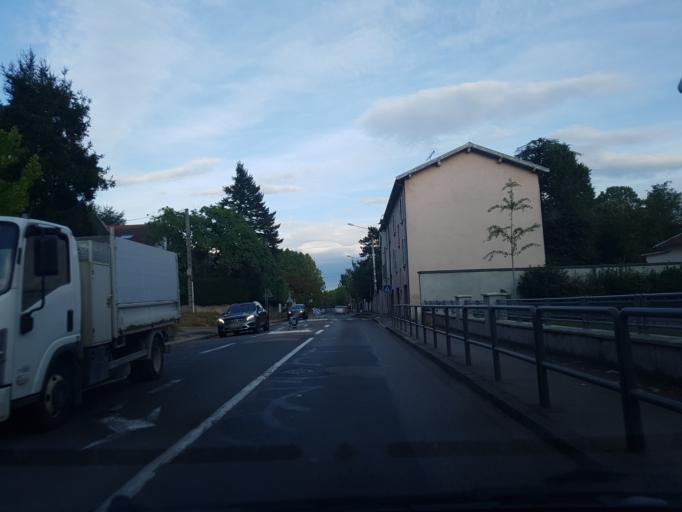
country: FR
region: Rhone-Alpes
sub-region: Departement du Rhone
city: Ecully
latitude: 45.7639
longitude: 4.7613
